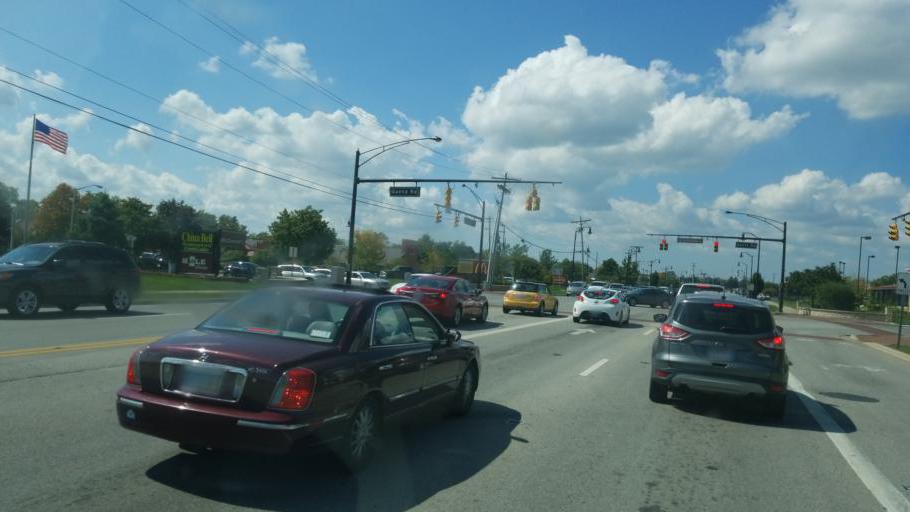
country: US
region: Ohio
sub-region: Franklin County
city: Grove City
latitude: 39.8784
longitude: -83.0551
